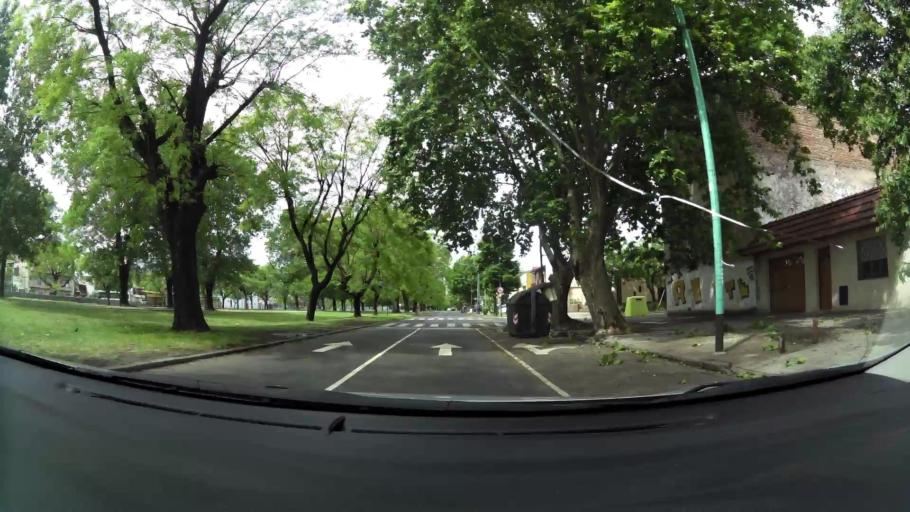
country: AR
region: Buenos Aires F.D.
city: Villa Lugano
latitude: -34.6610
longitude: -58.4299
